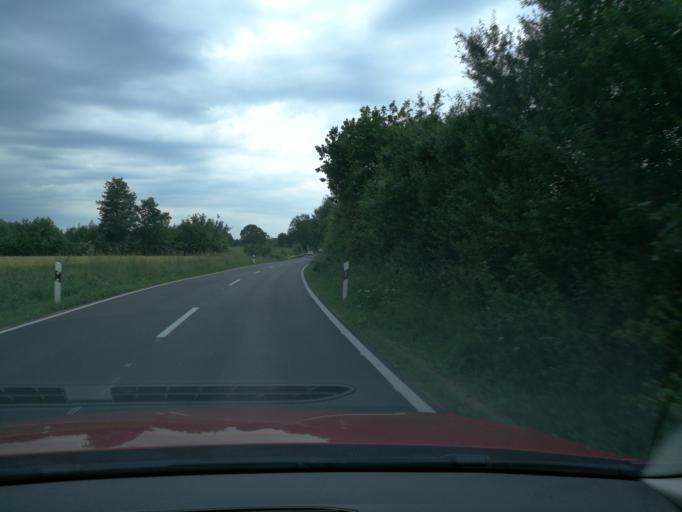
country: DE
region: Schleswig-Holstein
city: Lasbek
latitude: 53.7303
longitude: 10.3616
